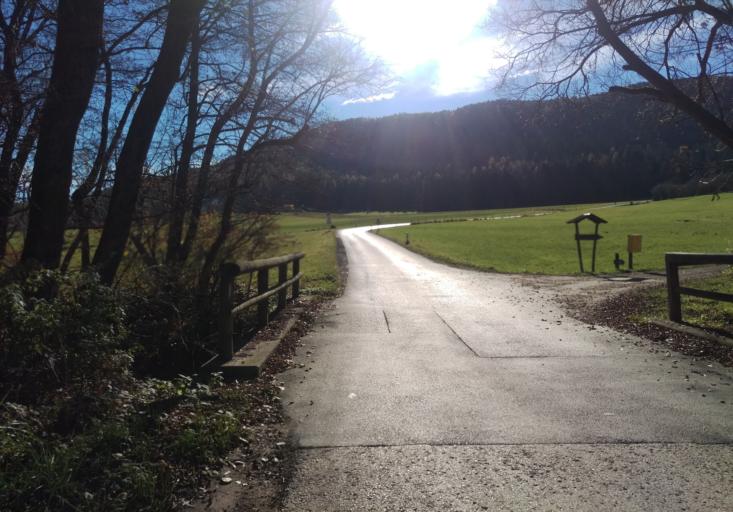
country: AT
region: Styria
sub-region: Politischer Bezirk Graz-Umgebung
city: Sankt Radegund bei Graz
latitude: 47.1338
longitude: 15.4862
